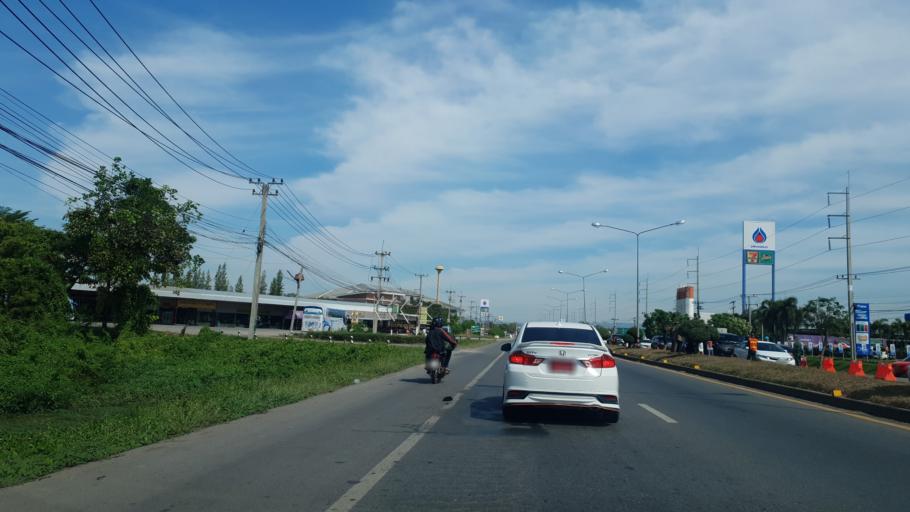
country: TH
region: Phitsanulok
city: Wang Thong
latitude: 16.8534
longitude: 100.3487
